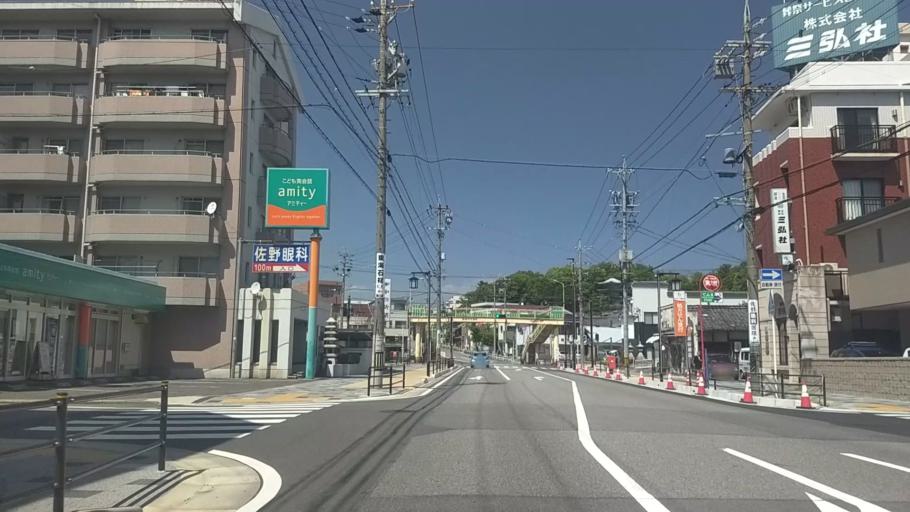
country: JP
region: Aichi
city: Okazaki
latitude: 34.9578
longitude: 137.1706
